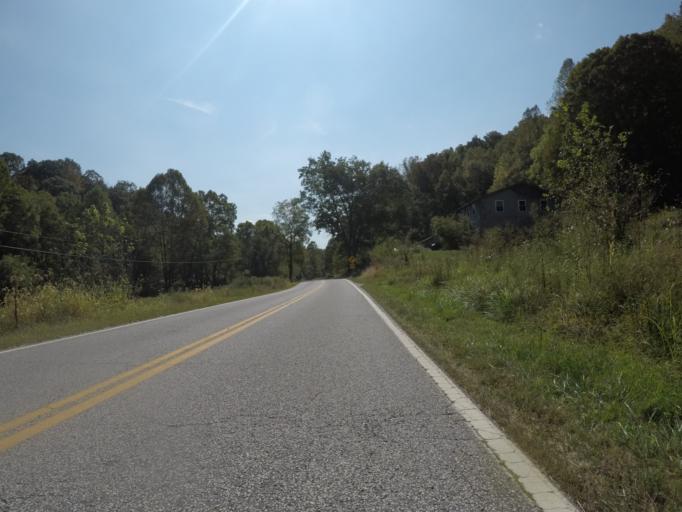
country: US
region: West Virginia
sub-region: Cabell County
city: Lesage
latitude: 38.5624
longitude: -82.3950
